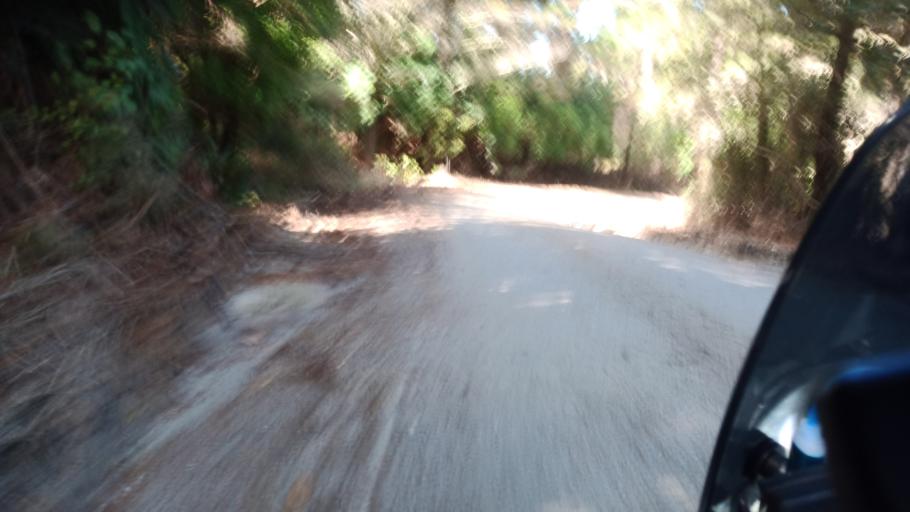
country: NZ
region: Gisborne
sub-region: Gisborne District
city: Gisborne
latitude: -38.8728
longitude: 177.7889
